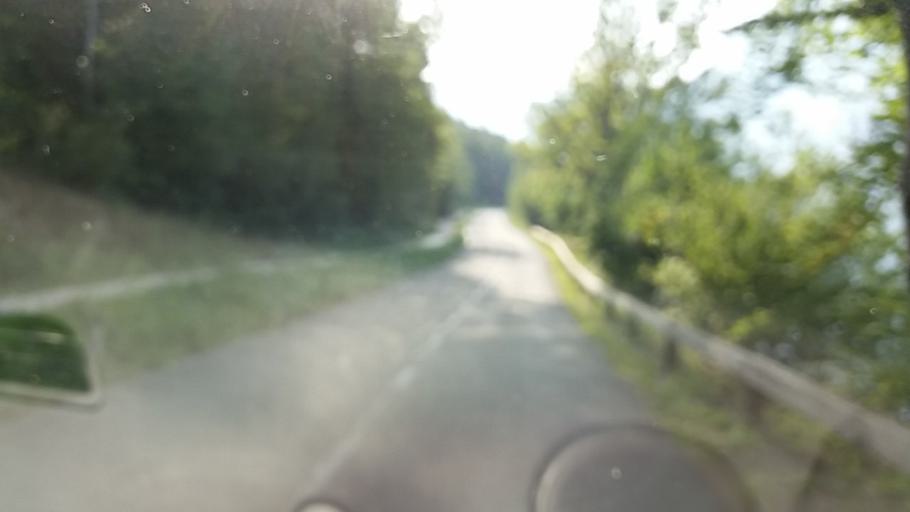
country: SI
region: Bohinj
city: Bohinjska Bistrica
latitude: 46.2776
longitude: 13.8800
